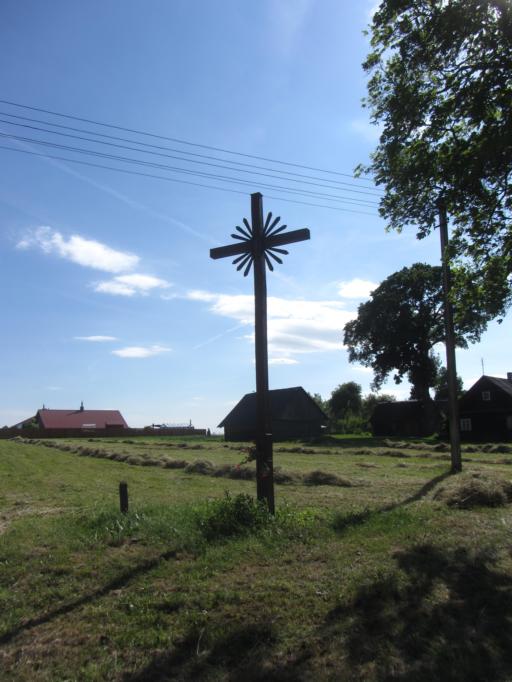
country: LT
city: Birstonas
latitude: 54.5700
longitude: 24.0783
